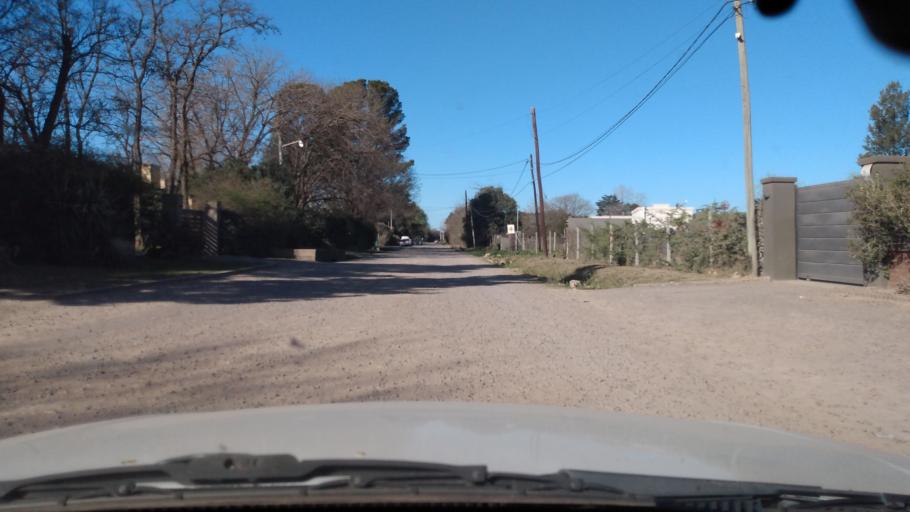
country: AR
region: Buenos Aires
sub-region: Partido de Mercedes
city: Mercedes
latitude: -34.6488
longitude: -59.4044
